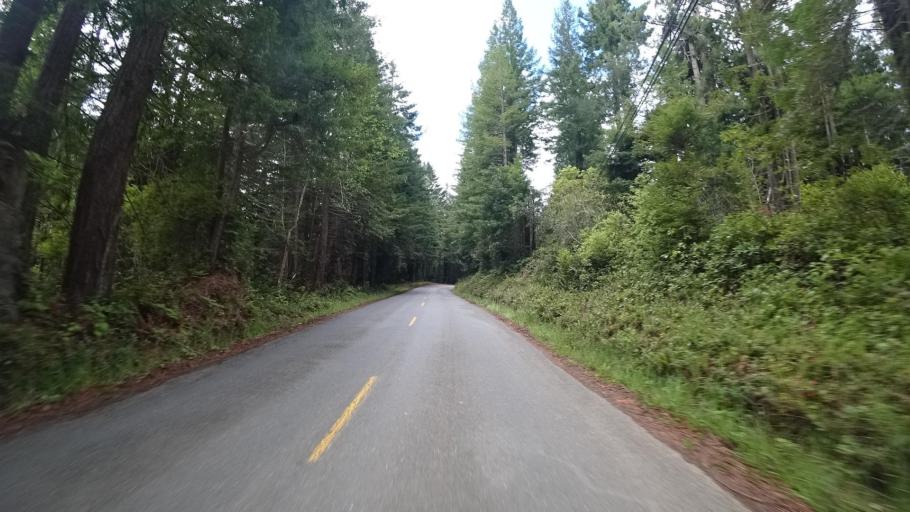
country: US
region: California
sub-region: Humboldt County
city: Bayside
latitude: 40.7961
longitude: -124.0544
